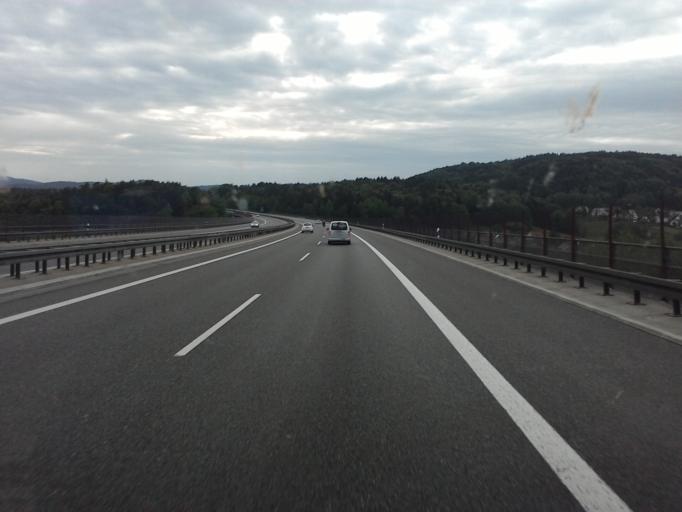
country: DE
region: Bavaria
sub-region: Upper Palatinate
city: Pilsach
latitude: 49.3148
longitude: 11.5078
